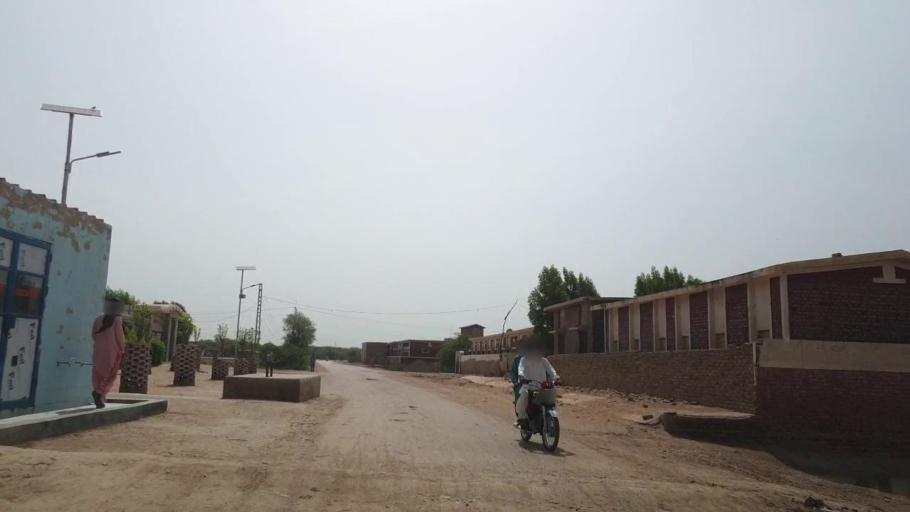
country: PK
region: Sindh
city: Nawabshah
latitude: 26.1177
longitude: 68.4029
